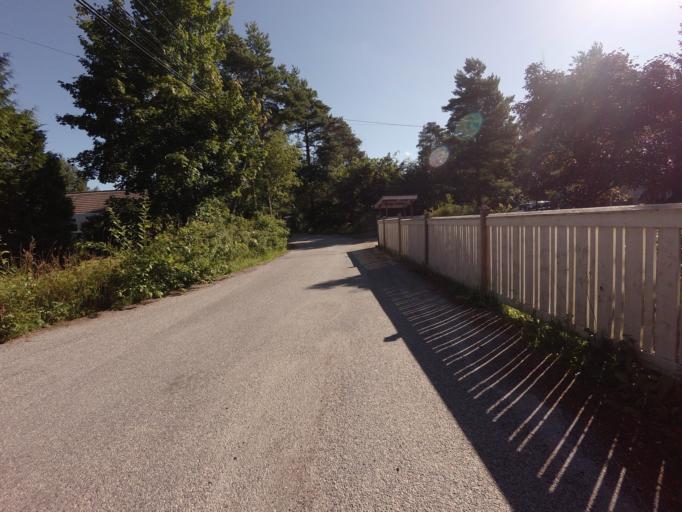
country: FI
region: Uusimaa
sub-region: Helsinki
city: Espoo
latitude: 60.1615
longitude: 24.6697
